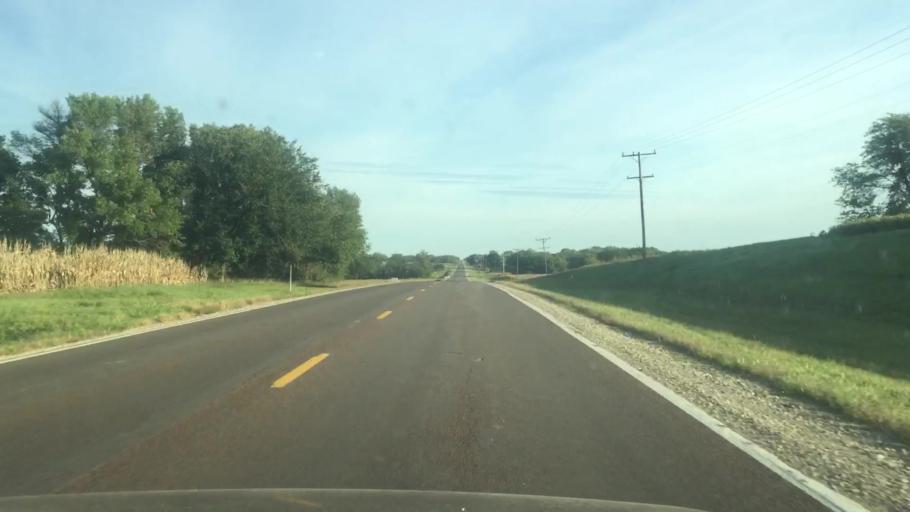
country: US
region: Kansas
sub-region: Marshall County
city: Marysville
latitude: 39.9645
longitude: -96.6572
